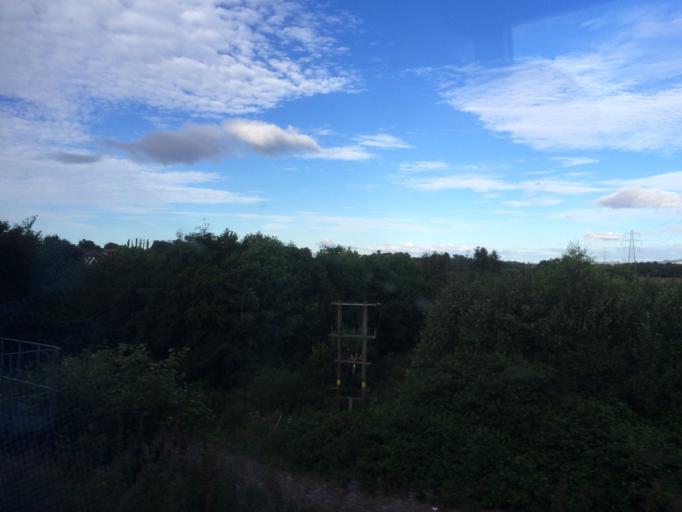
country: GB
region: Scotland
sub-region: Falkirk
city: Larbert
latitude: 56.0151
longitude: -3.8326
